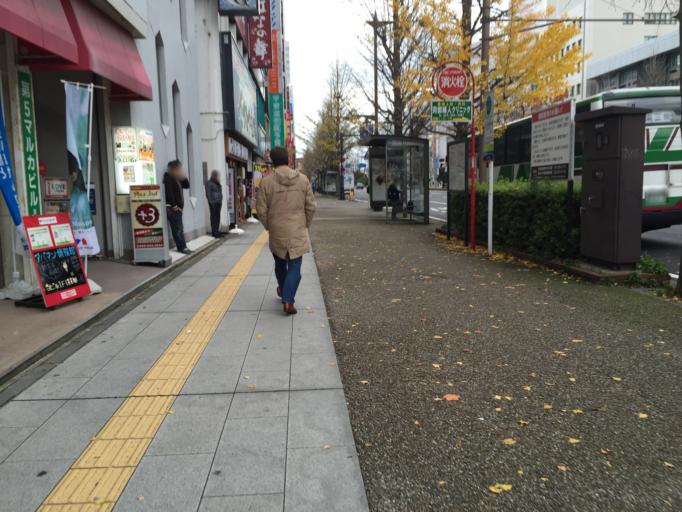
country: JP
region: Niigata
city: Niigata-shi
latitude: 37.9136
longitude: 139.0610
